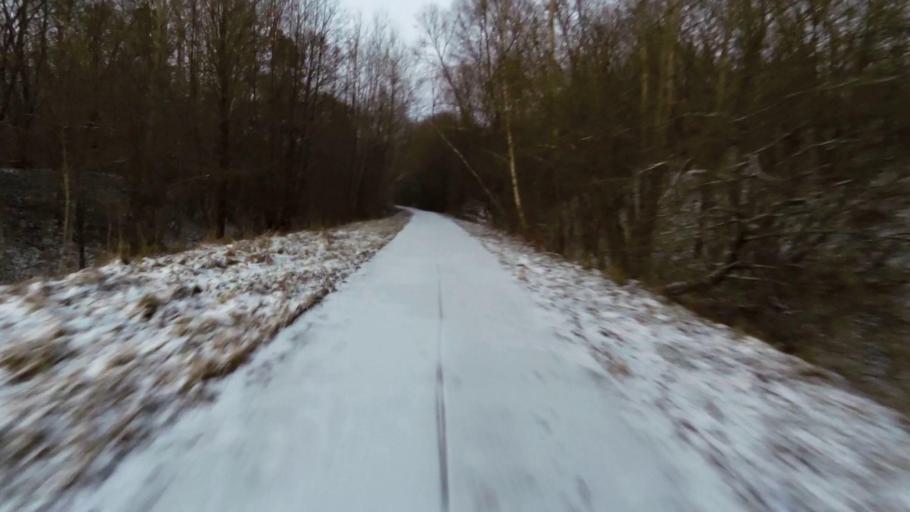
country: PL
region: West Pomeranian Voivodeship
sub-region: Powiat swidwinski
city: Polczyn-Zdroj
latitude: 53.7377
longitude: 16.0492
